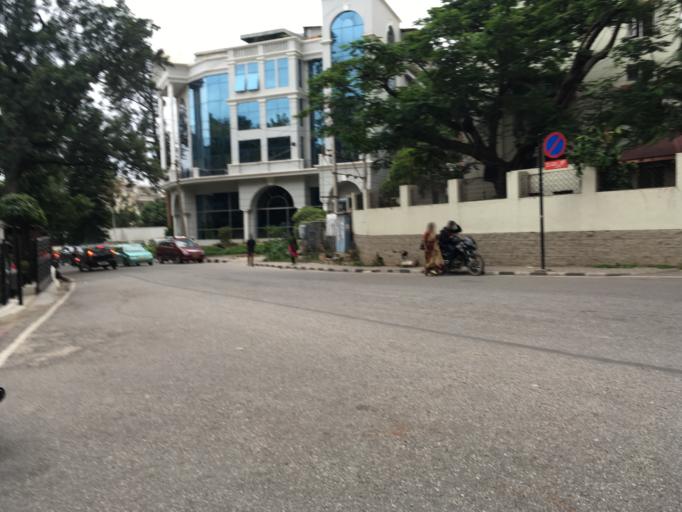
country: IN
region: Karnataka
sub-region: Bangalore Urban
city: Bangalore
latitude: 12.9728
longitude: 77.5993
